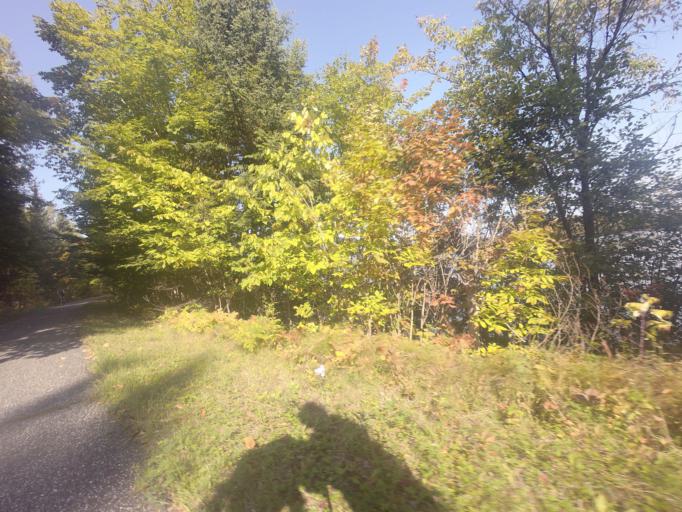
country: CA
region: Quebec
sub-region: Laurentides
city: Mont-Laurier
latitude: 46.5075
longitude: -75.3985
